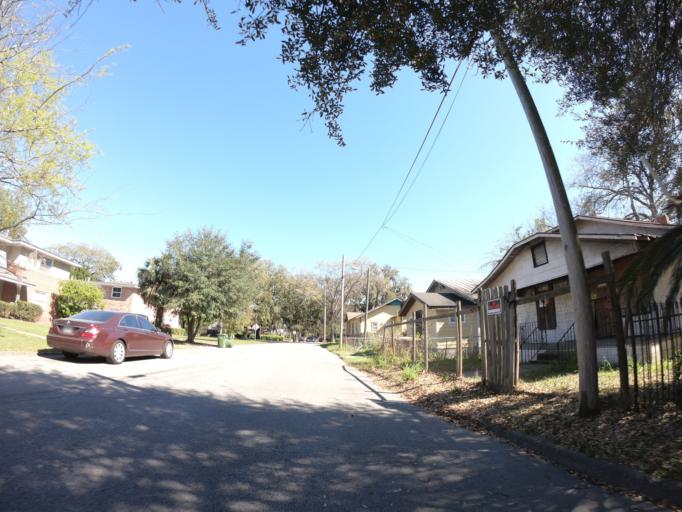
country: US
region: Georgia
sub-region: Chatham County
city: Savannah
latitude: 32.0454
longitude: -81.1055
